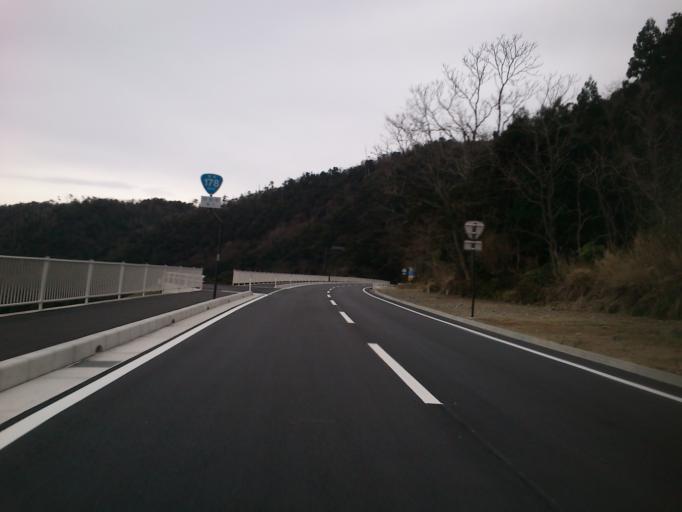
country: JP
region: Kyoto
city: Miyazu
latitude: 35.7460
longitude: 135.2547
